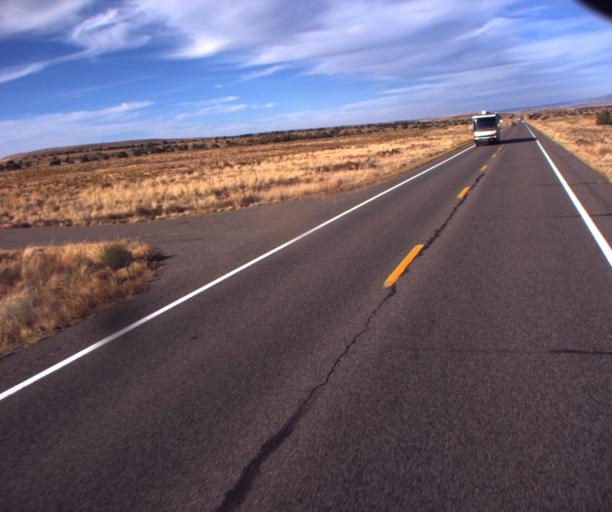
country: US
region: Colorado
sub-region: Montezuma County
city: Towaoc
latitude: 36.9658
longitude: -109.0640
